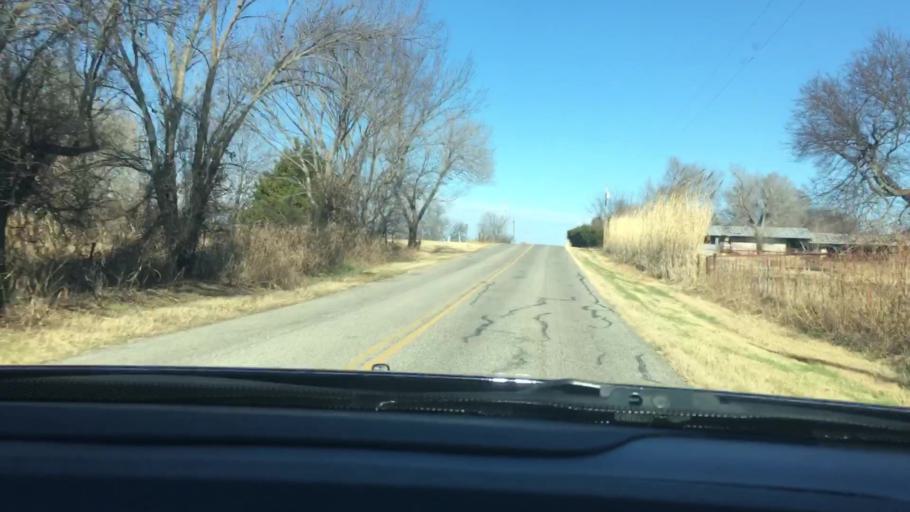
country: US
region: Oklahoma
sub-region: Murray County
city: Davis
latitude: 34.4967
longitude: -97.0554
